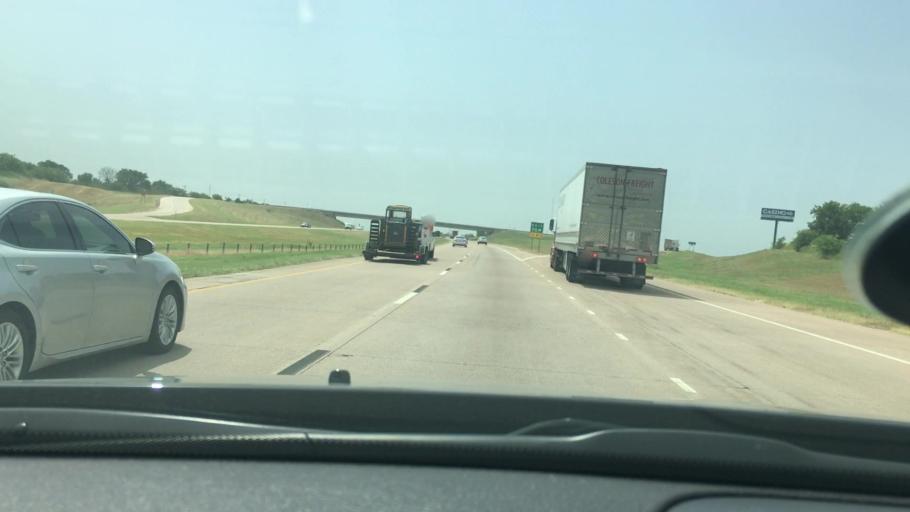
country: US
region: Oklahoma
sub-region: Garvin County
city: Pauls Valley
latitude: 34.7094
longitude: -97.2477
